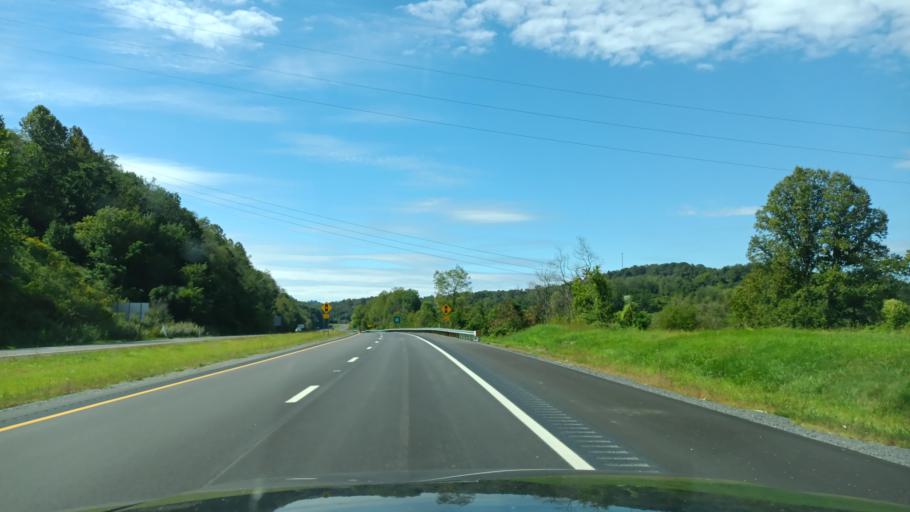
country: US
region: West Virginia
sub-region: Harrison County
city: Clarksburg
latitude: 39.2859
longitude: -80.3858
